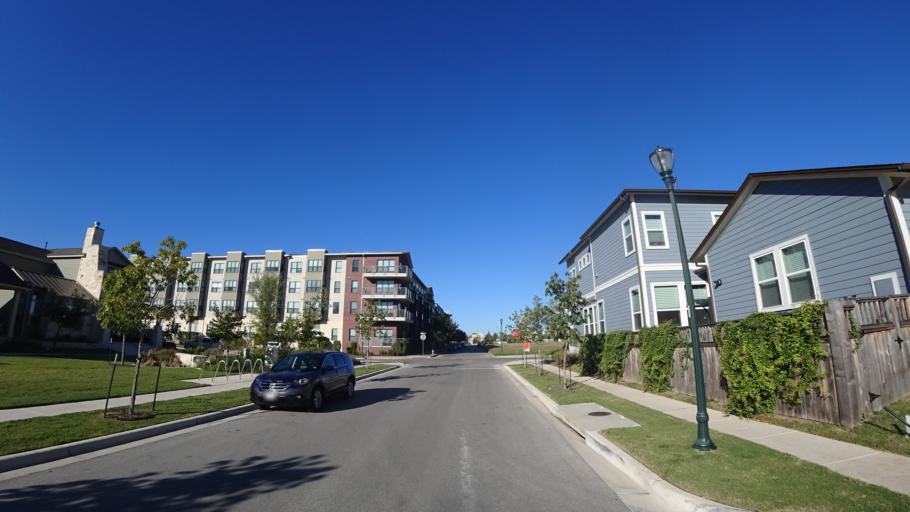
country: US
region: Texas
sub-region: Travis County
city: Austin
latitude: 30.2912
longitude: -97.6970
